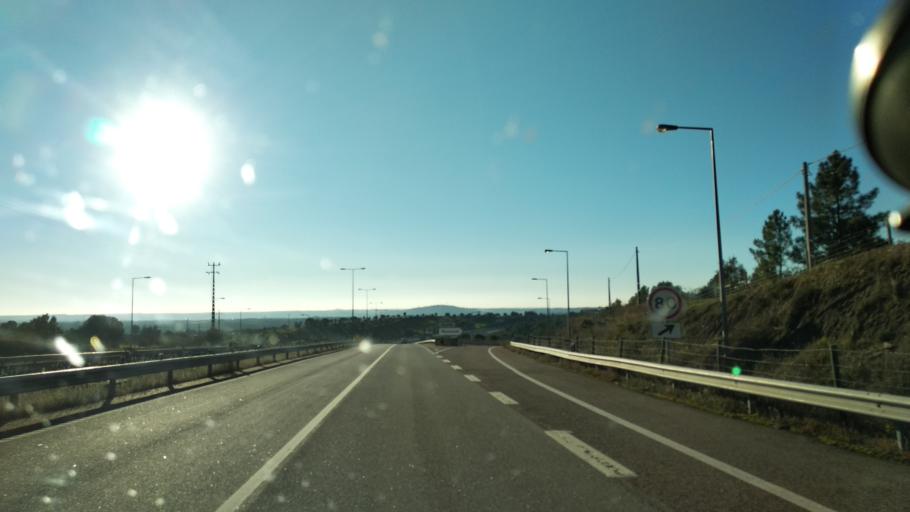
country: PT
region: Santarem
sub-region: Abrantes
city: Alferrarede
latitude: 39.4945
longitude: -8.0951
